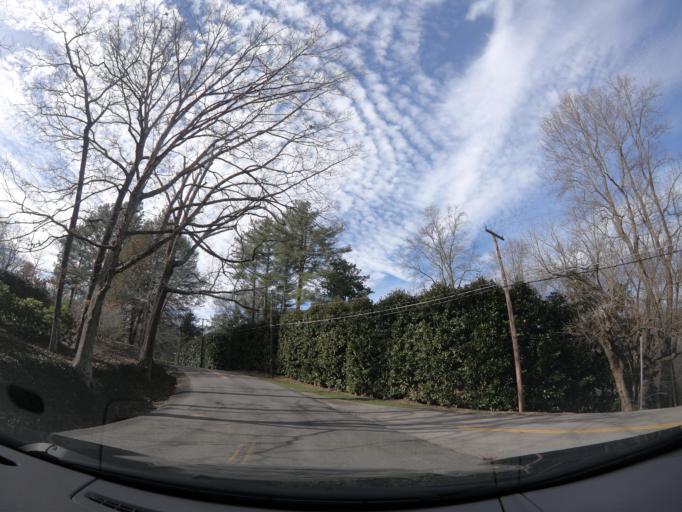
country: US
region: Tennessee
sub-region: Hamilton County
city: Lookout Mountain
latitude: 34.9865
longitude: -85.3481
